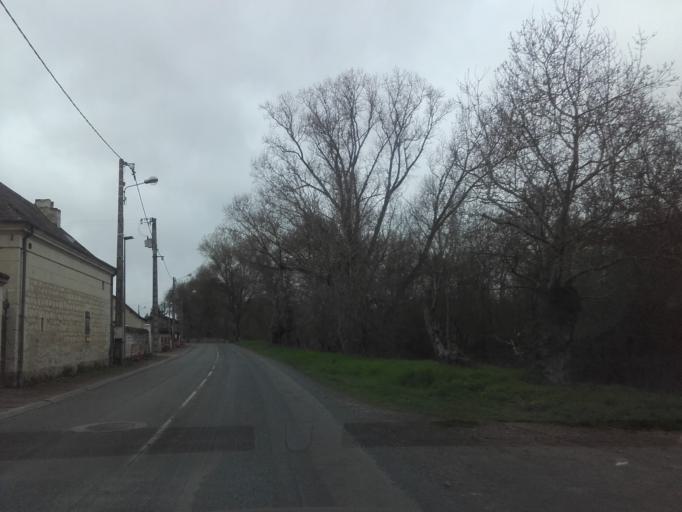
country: FR
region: Centre
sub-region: Departement d'Indre-et-Loire
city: La Chapelle-sur-Loire
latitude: 47.2319
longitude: 0.2012
